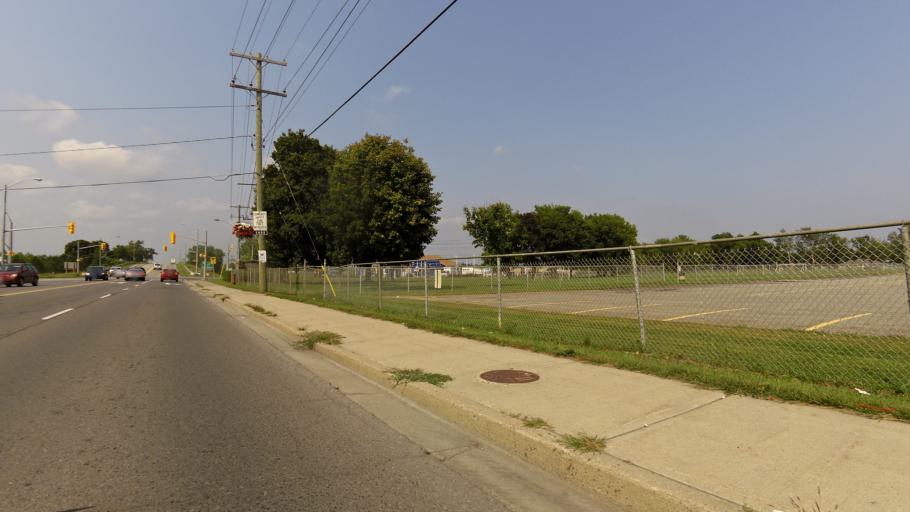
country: CA
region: Ontario
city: Prescott
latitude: 44.7203
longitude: -75.5228
